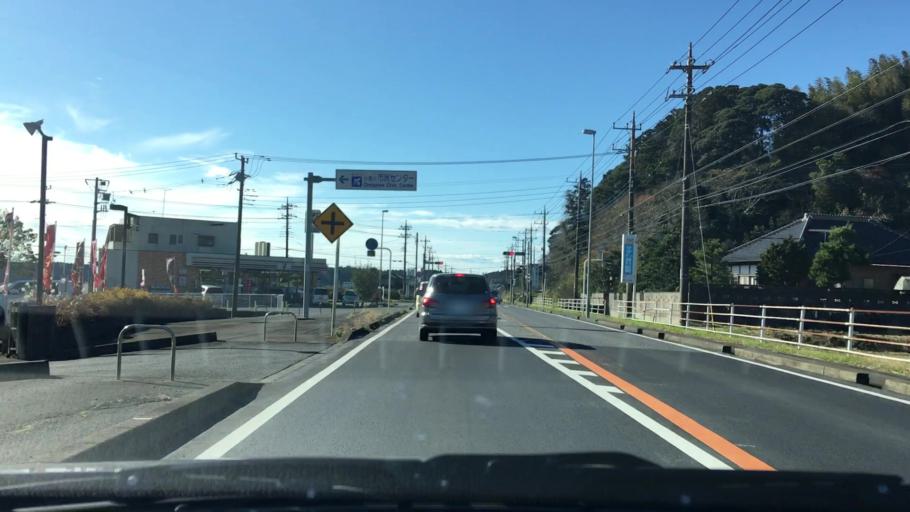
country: JP
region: Chiba
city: Omigawa
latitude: 35.8508
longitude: 140.5810
